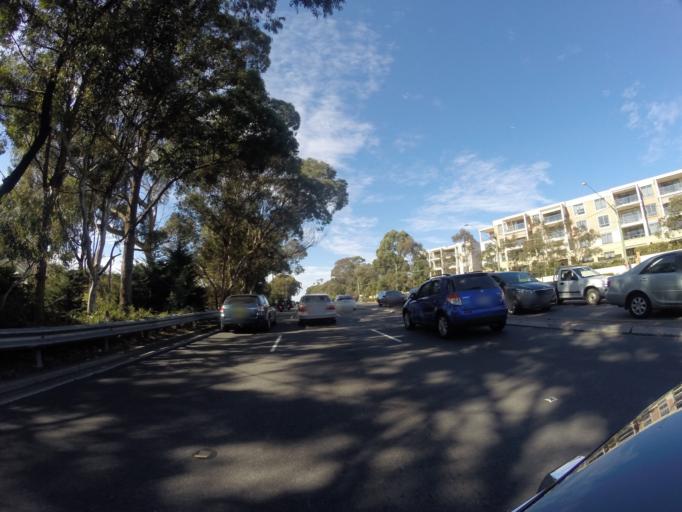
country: AU
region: New South Wales
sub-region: Sutherland Shire
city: Kirrawee
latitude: -34.0316
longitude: 151.0672
